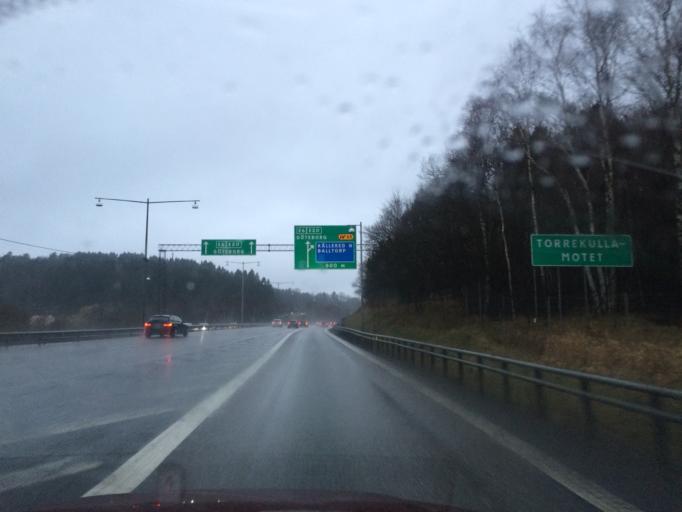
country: SE
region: Vaestra Goetaland
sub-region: Molndal
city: Kallered
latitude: 57.6192
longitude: 12.0397
